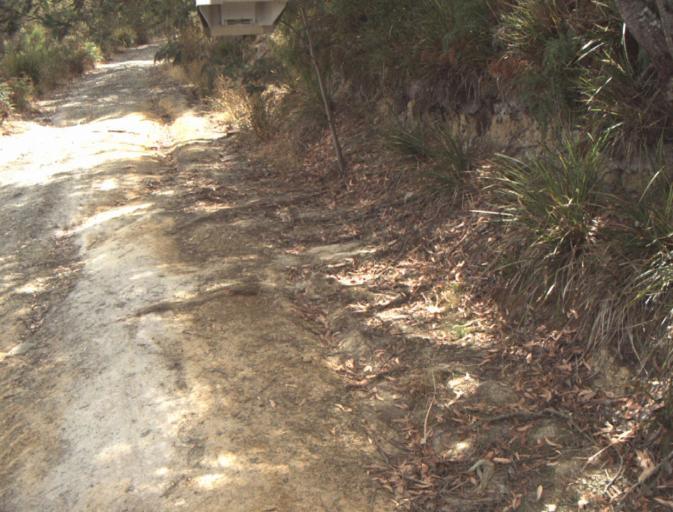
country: AU
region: Tasmania
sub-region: Launceston
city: Mayfield
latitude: -41.2056
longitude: 147.1549
